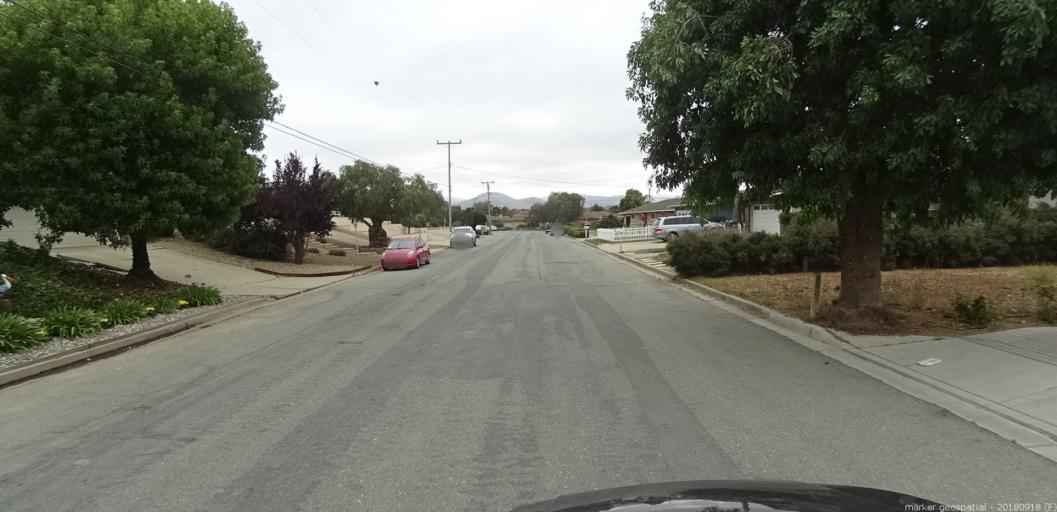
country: US
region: California
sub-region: Monterey County
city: Prunedale
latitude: 36.7356
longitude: -121.6415
